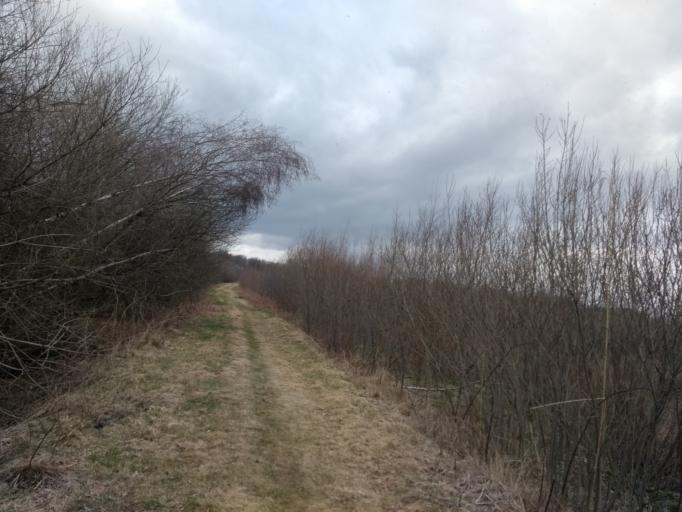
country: NL
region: Overijssel
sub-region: Gemeente Haaksbergen
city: Haaksbergen
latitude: 52.1196
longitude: 6.7731
